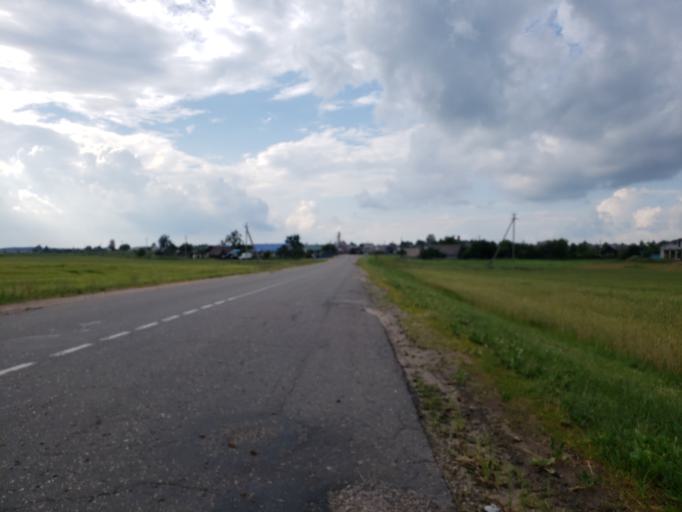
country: BY
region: Minsk
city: Chervyen'
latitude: 53.7278
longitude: 28.3902
